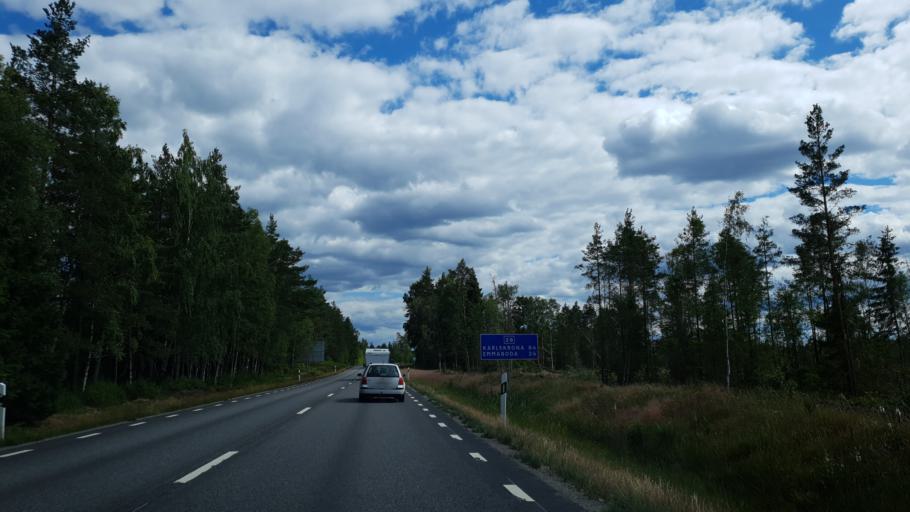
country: SE
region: Kronoberg
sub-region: Lessebo Kommun
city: Lessebo
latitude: 56.8297
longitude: 15.3985
